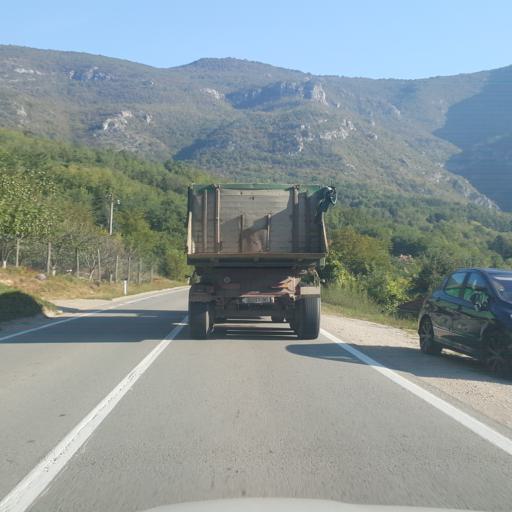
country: RS
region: Central Serbia
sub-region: Nisavski Okrug
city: Svrljig
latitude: 43.3313
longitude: 22.1162
